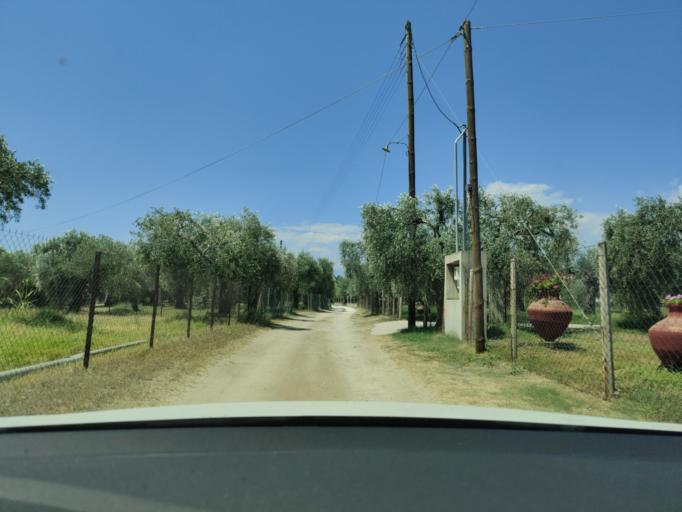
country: GR
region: East Macedonia and Thrace
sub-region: Nomos Kavalas
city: Prinos
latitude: 40.7696
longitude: 24.5963
